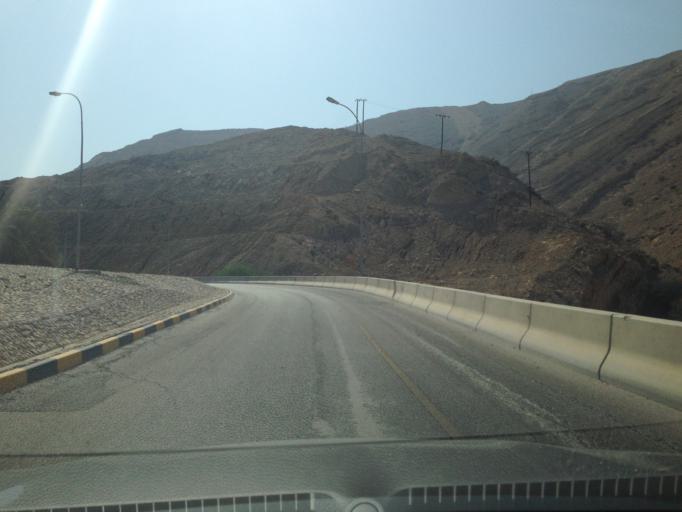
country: OM
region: Muhafazat Masqat
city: Muscat
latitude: 23.5598
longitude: 58.5956
